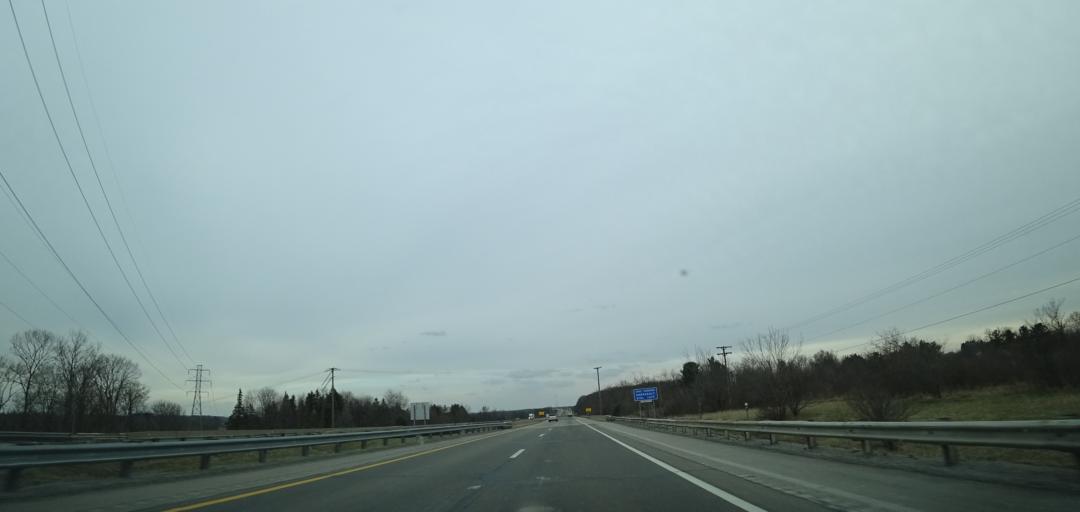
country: US
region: Ohio
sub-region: Mahoning County
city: New Middletown
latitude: 40.9363
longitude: -80.5774
